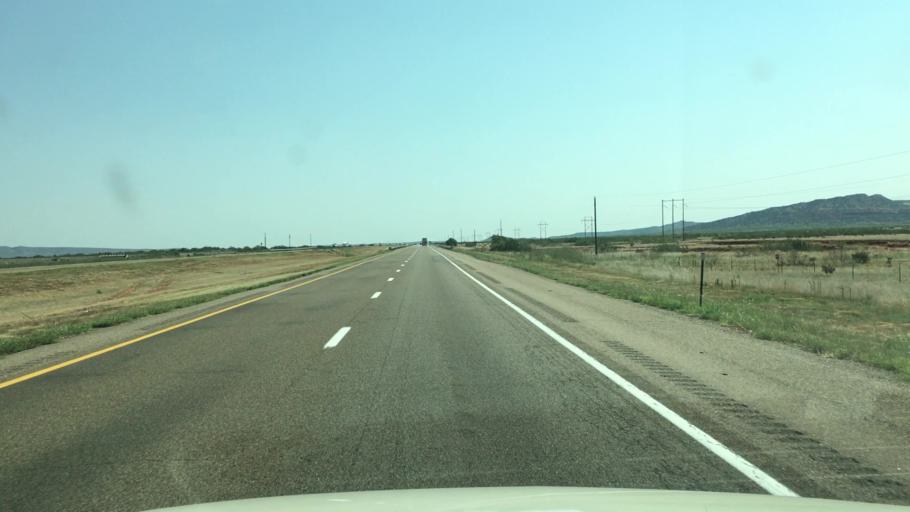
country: US
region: New Mexico
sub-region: Quay County
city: Tucumcari
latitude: 35.1018
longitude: -104.0411
